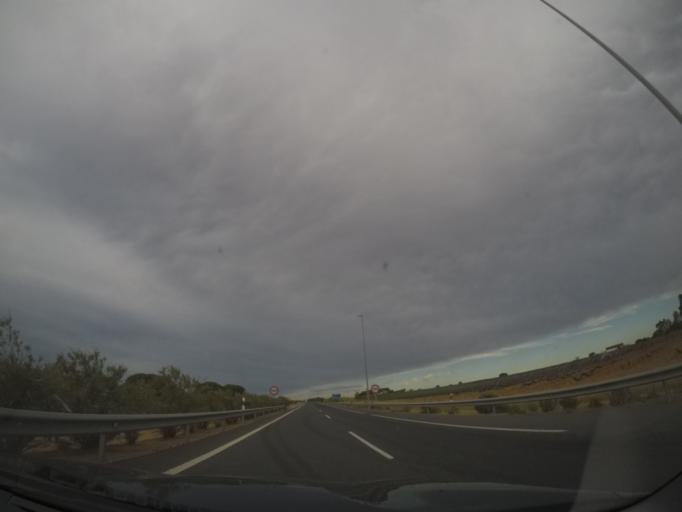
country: ES
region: Andalusia
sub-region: Provincia de Huelva
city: Lepe
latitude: 37.2952
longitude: -7.2229
